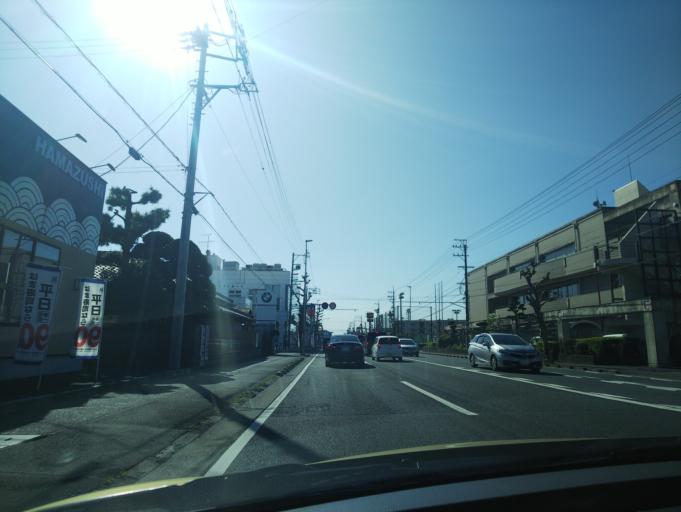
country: JP
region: Shizuoka
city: Shizuoka-shi
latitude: 34.9527
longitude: 138.3852
